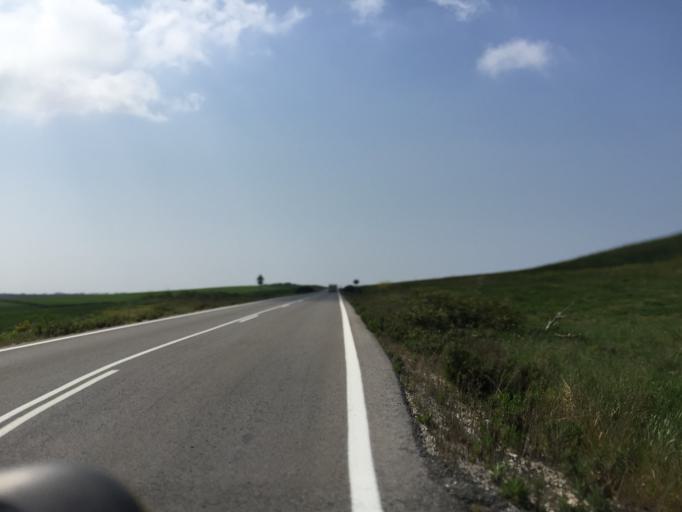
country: ES
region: Andalusia
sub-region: Provincia de Cadiz
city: Vejer de la Frontera
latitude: 36.2346
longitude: -6.0295
